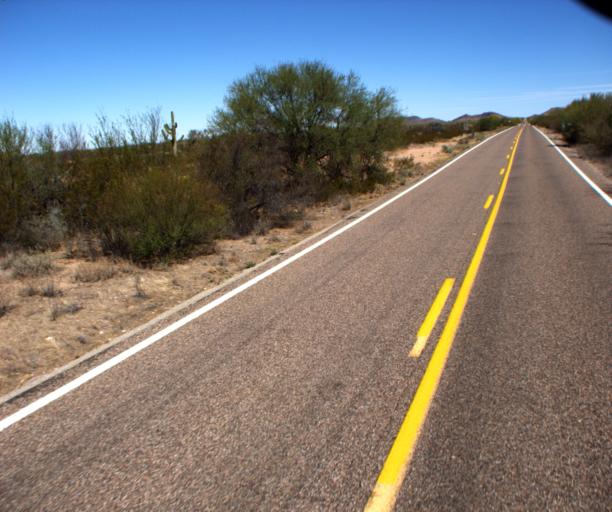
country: MX
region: Sonora
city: Sonoyta
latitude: 32.0414
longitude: -112.7949
